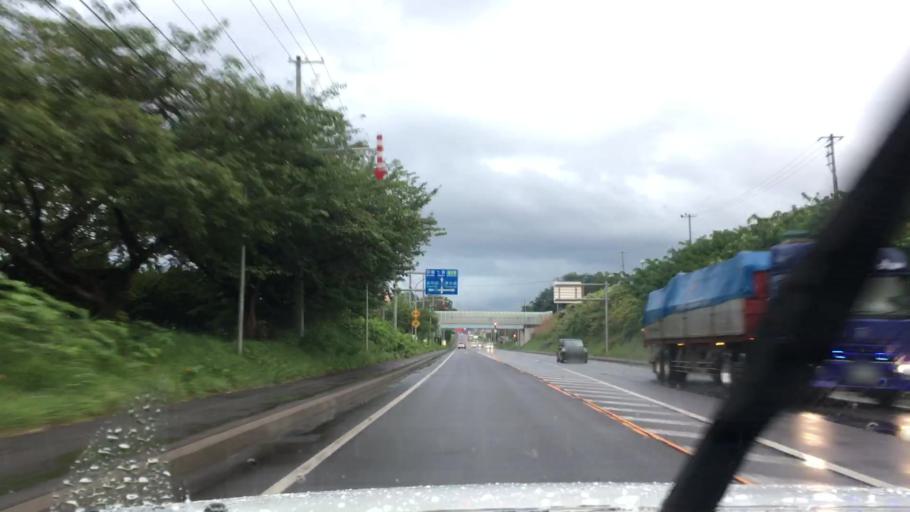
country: JP
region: Hokkaido
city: Nanae
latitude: 42.0982
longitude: 140.5689
